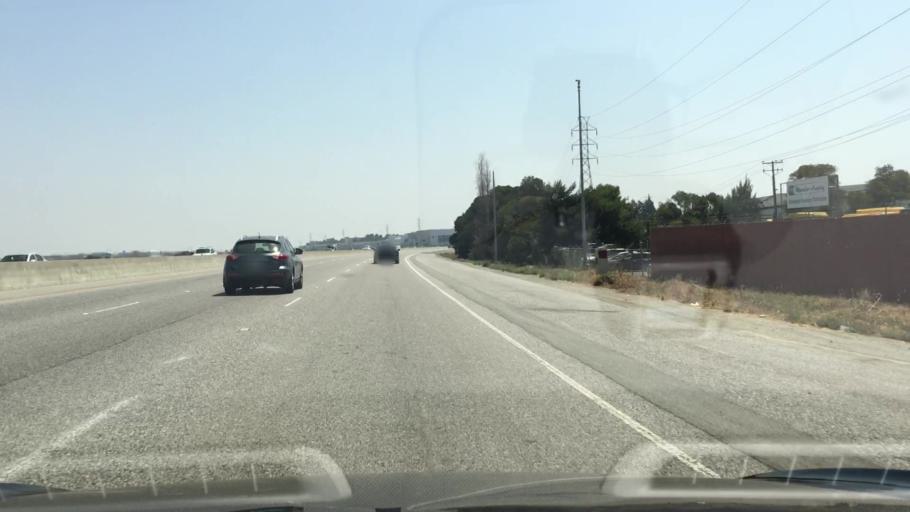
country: US
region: California
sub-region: San Mateo County
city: North Fair Oaks
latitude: 37.4850
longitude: -122.1730
